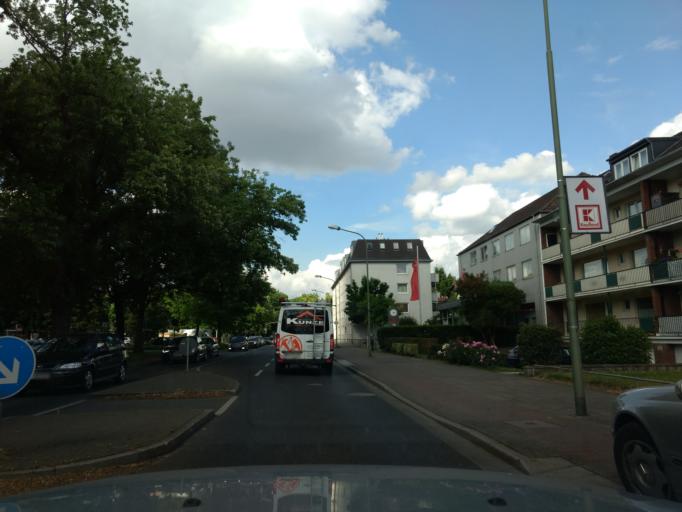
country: DE
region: North Rhine-Westphalia
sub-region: Regierungsbezirk Dusseldorf
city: Neuss
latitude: 51.2077
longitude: 6.6726
